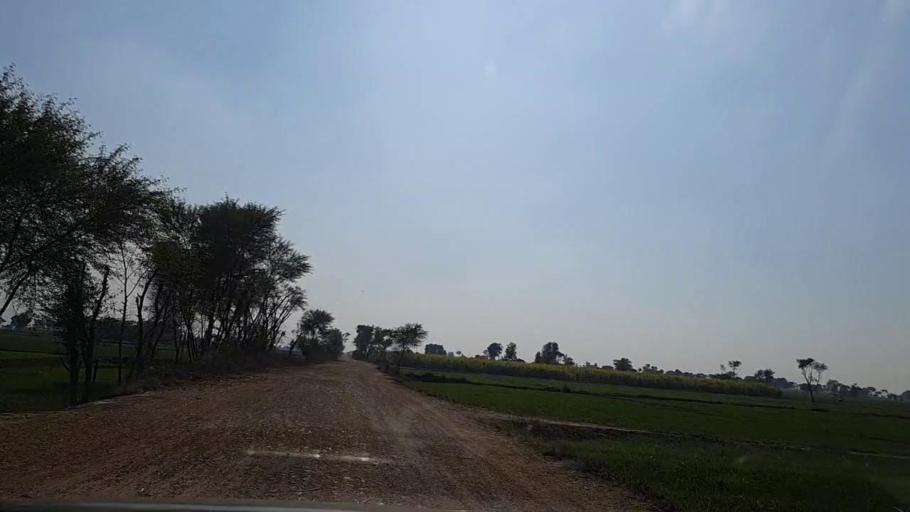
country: PK
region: Sindh
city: Daulatpur
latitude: 26.2889
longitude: 68.0537
